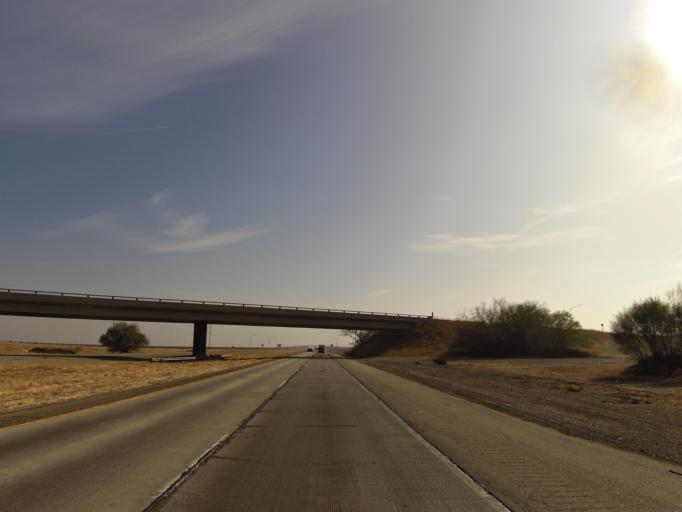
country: US
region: California
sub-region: Kern County
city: Greenfield
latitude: 35.1620
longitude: -119.1114
